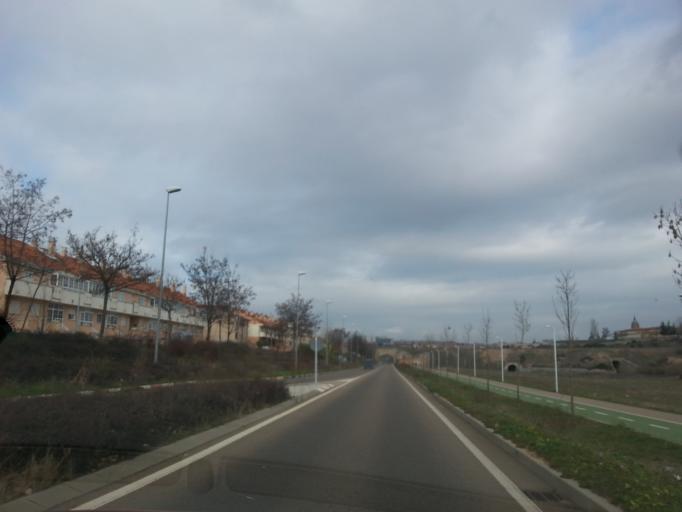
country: ES
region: Castille and Leon
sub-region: Provincia de Salamanca
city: Salamanca
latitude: 40.9492
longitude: -5.6777
